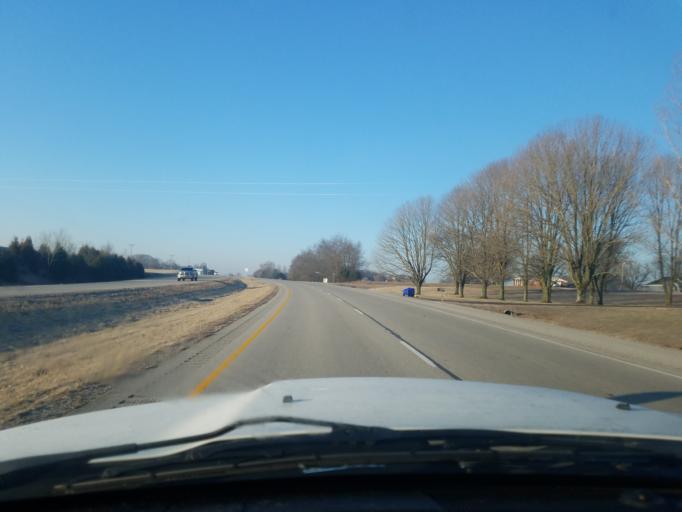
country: US
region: Kentucky
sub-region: Logan County
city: Auburn
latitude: 36.9081
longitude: -86.5840
